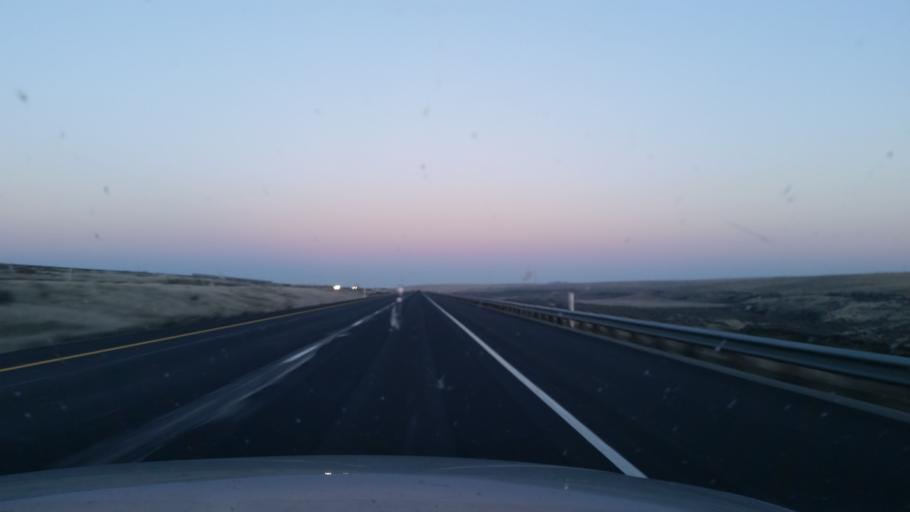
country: US
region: Washington
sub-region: Adams County
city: Ritzville
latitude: 47.0984
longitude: -118.6160
